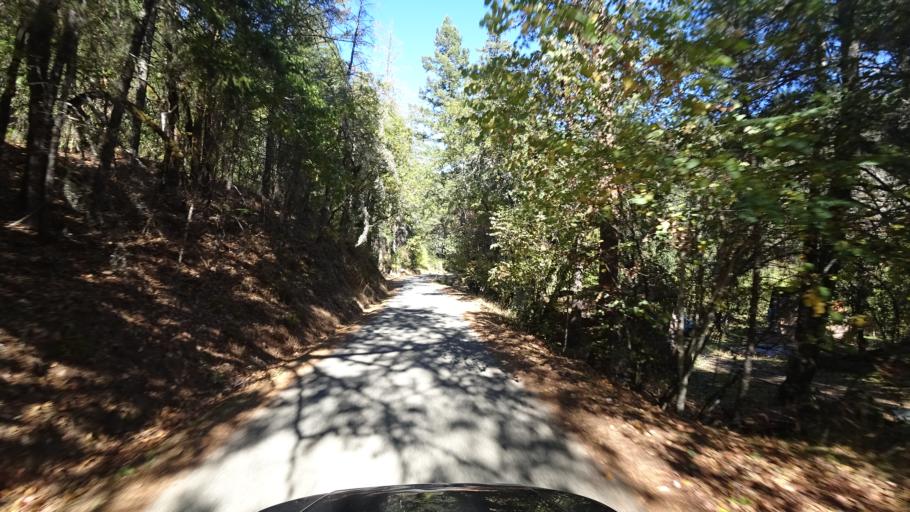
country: US
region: California
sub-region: Humboldt County
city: Willow Creek
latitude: 41.2454
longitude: -123.2994
